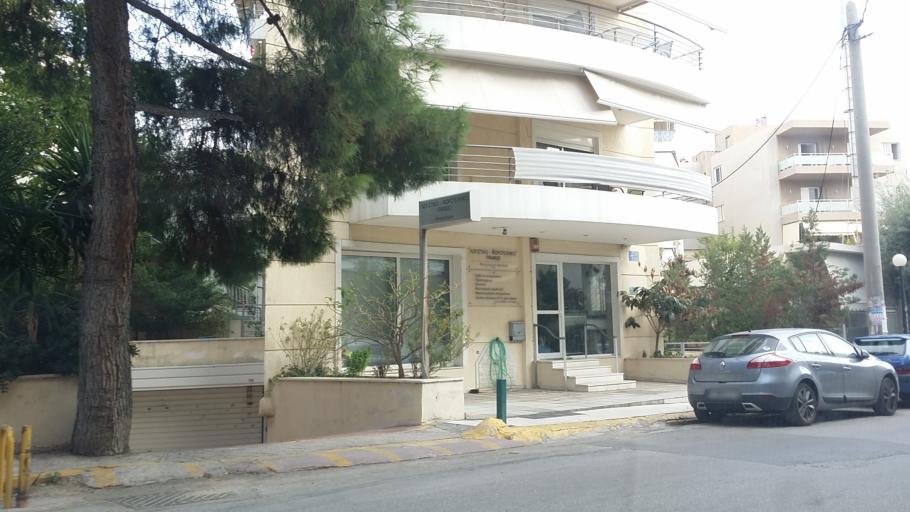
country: GR
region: Attica
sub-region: Nomarchia Athinas
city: Irakleio
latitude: 38.0516
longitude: 23.7623
